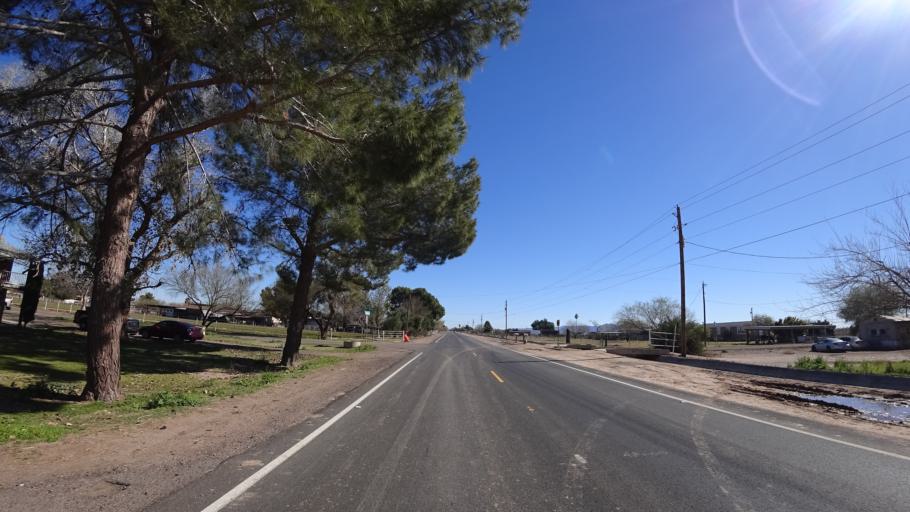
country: US
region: Arizona
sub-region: Maricopa County
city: Tolleson
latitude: 33.3919
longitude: -112.2936
